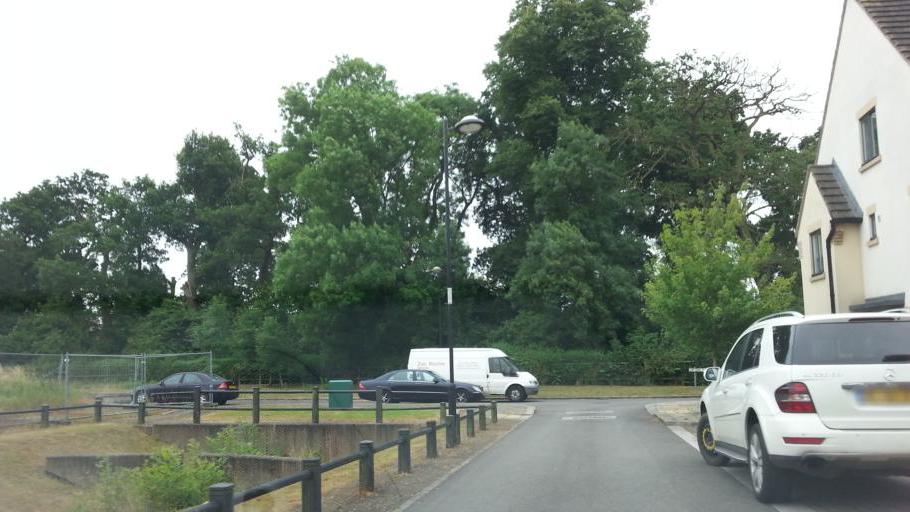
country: GB
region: England
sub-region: Northamptonshire
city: Blisworth
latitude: 52.2321
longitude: -0.9457
